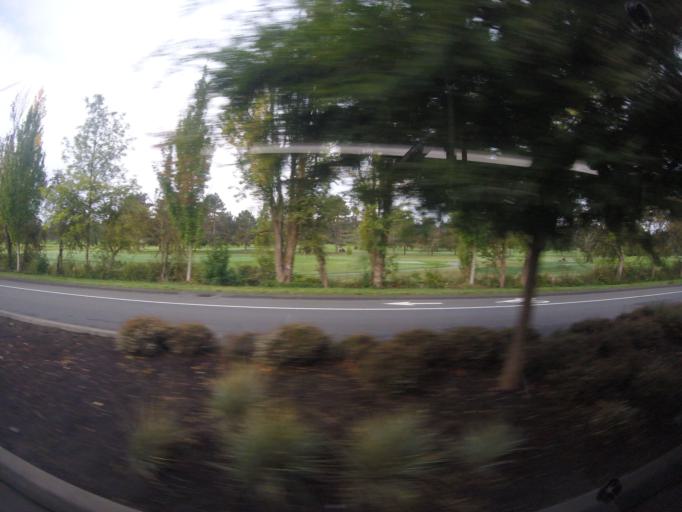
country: US
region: Washington
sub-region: King County
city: Medina
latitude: 47.6257
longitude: -122.2280
